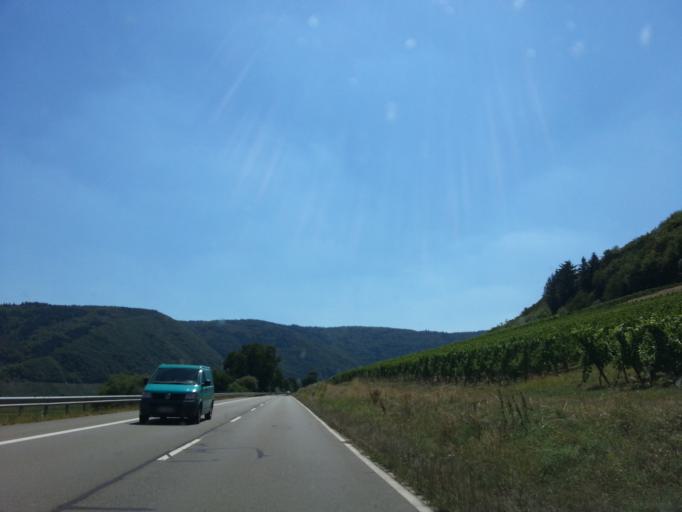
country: DE
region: Rheinland-Pfalz
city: Detzem
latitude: 49.8086
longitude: 6.8433
